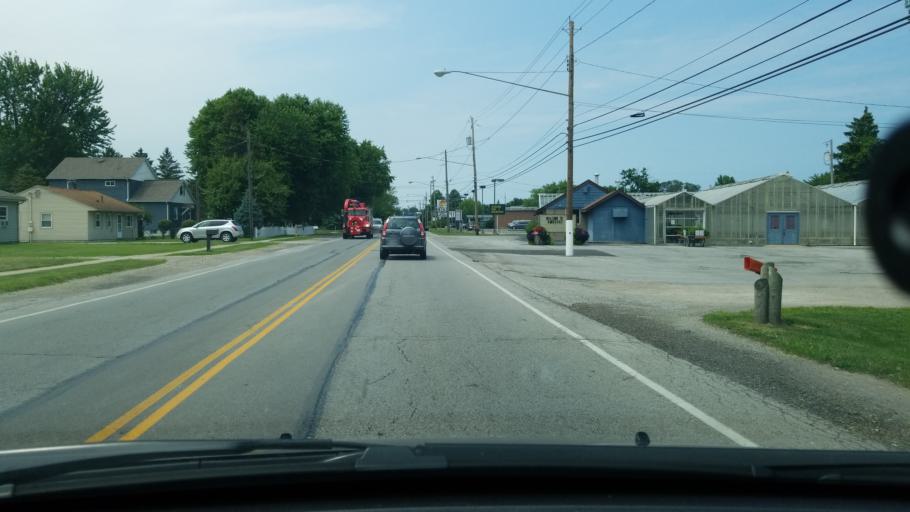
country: US
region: Ohio
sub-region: Erie County
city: Sandusky
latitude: 41.4387
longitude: -82.6734
